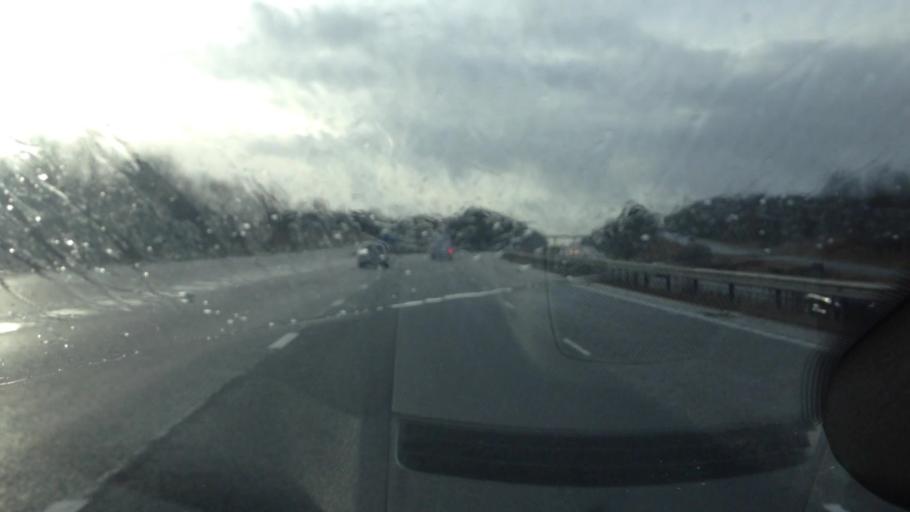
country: GB
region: England
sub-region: City and Borough of Wakefield
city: Crigglestone
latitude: 53.6281
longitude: -1.5414
